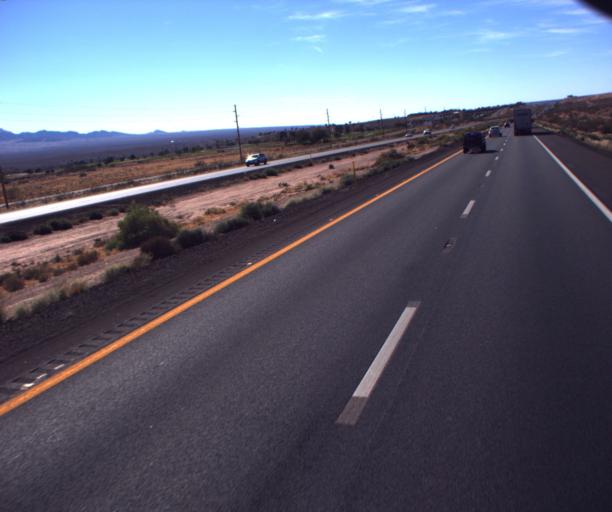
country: US
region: Nevada
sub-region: Clark County
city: Mesquite
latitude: 36.8236
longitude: -114.0296
